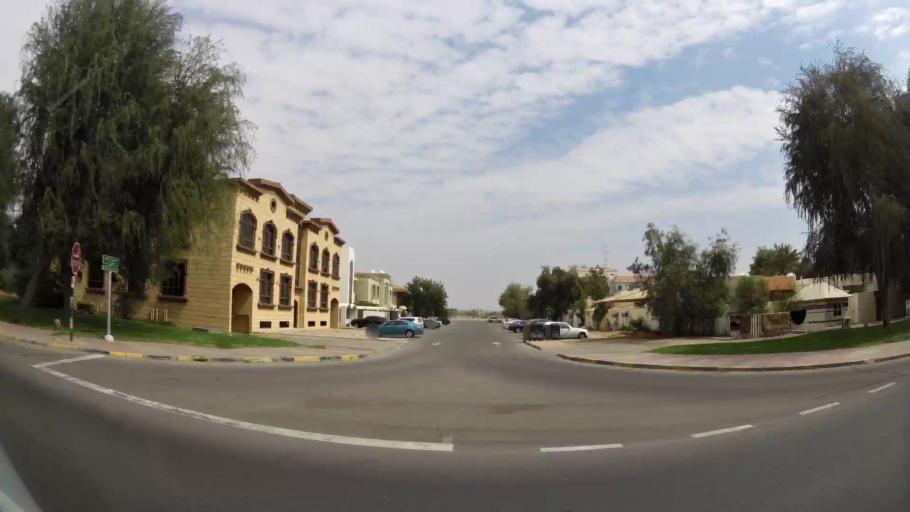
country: OM
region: Al Buraimi
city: Al Buraymi
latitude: 24.2283
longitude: 55.7842
